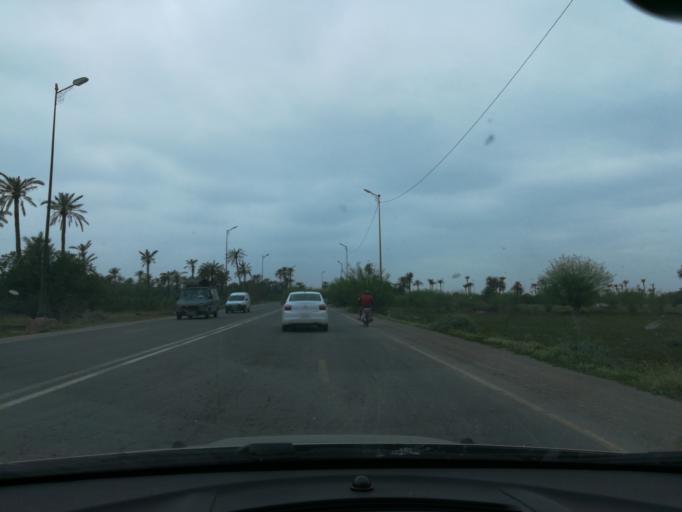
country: MA
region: Marrakech-Tensift-Al Haouz
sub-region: Marrakech
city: Marrakesh
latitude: 31.6885
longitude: -8.0208
